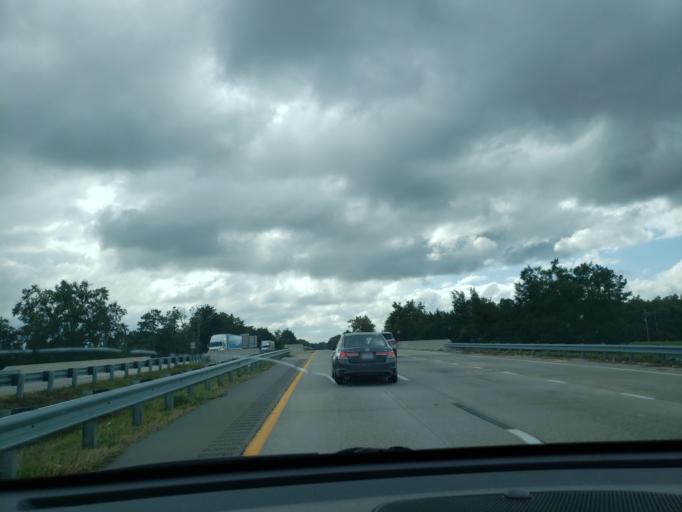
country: US
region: North Carolina
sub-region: Vance County
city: Henderson
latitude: 36.3936
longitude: -78.3379
